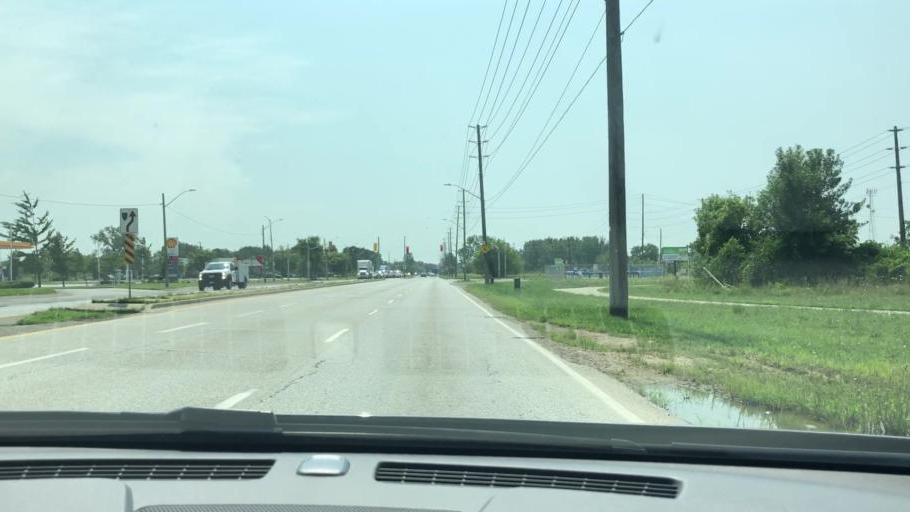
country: US
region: Michigan
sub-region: Wayne County
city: River Rouge
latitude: 42.2611
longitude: -83.0853
